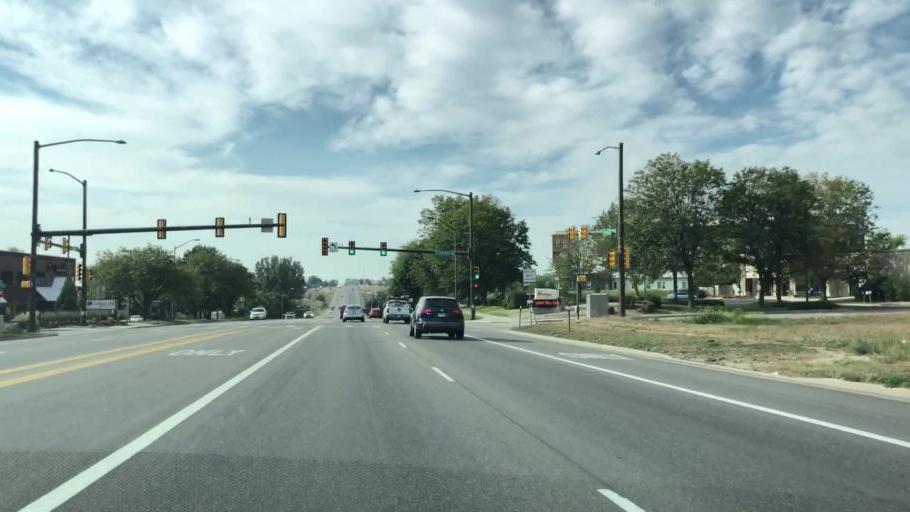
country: US
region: Colorado
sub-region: Larimer County
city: Fort Collins
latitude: 40.5180
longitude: -105.0772
